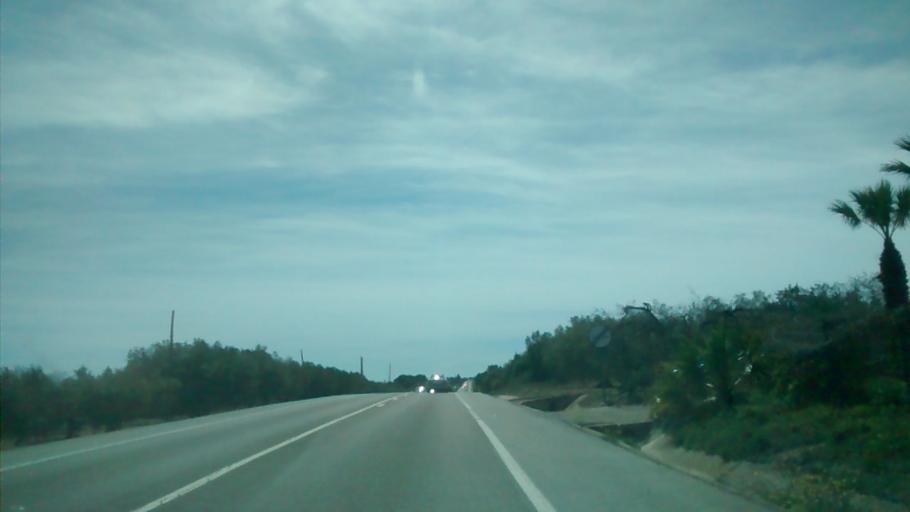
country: ES
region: Catalonia
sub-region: Provincia de Tarragona
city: Sant Carles de la Rapita
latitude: 40.6576
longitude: 0.5882
